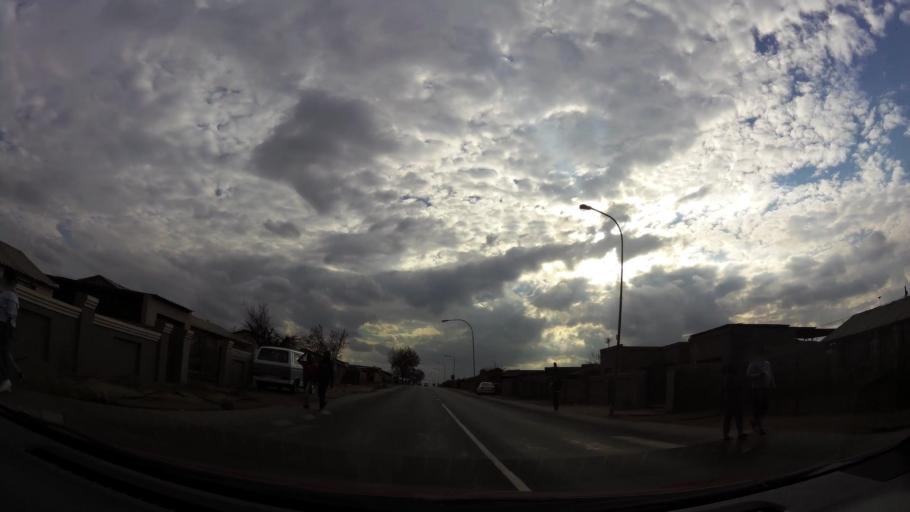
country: ZA
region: Gauteng
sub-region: City of Johannesburg Metropolitan Municipality
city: Soweto
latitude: -26.2538
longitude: 27.8277
